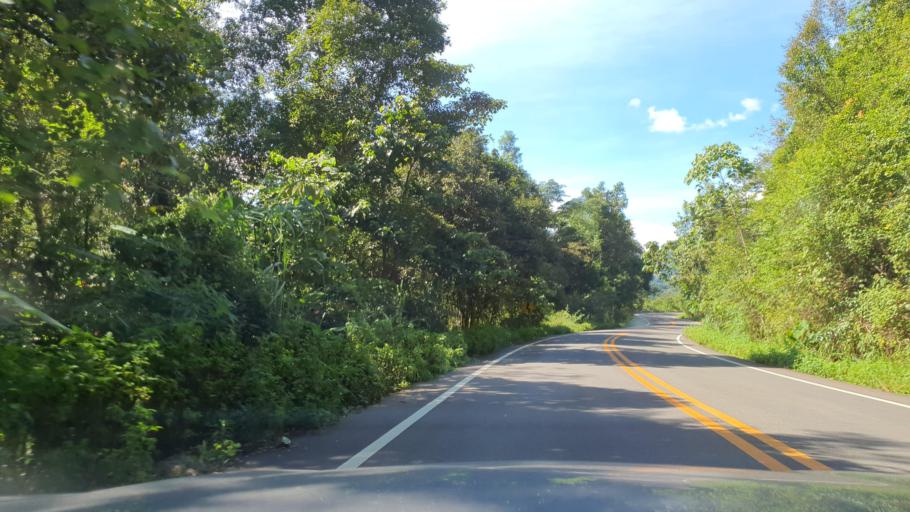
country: TH
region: Chiang Rai
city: Wiang Pa Pao
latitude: 19.3062
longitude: 99.3568
